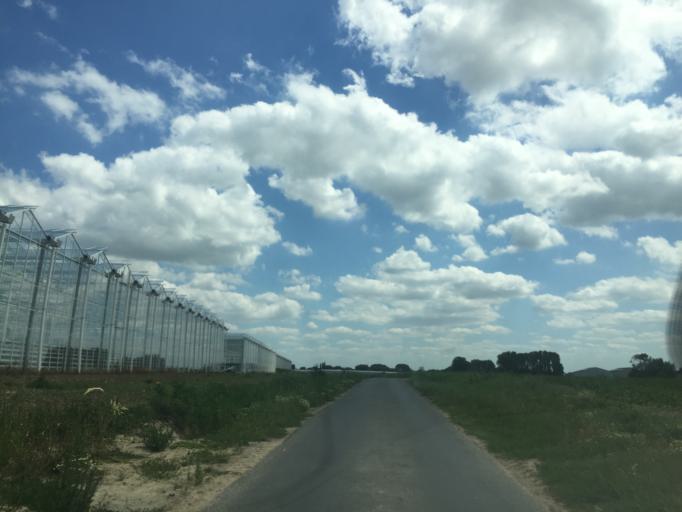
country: BE
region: Flanders
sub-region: Provincie West-Vlaanderen
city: Staden
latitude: 50.9970
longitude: 3.0073
